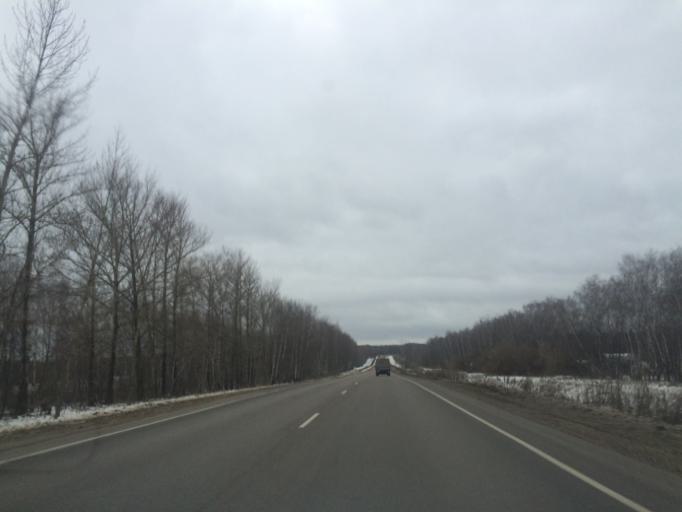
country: RU
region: Tula
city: Pervomayskiy
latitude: 54.1393
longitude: 37.3788
